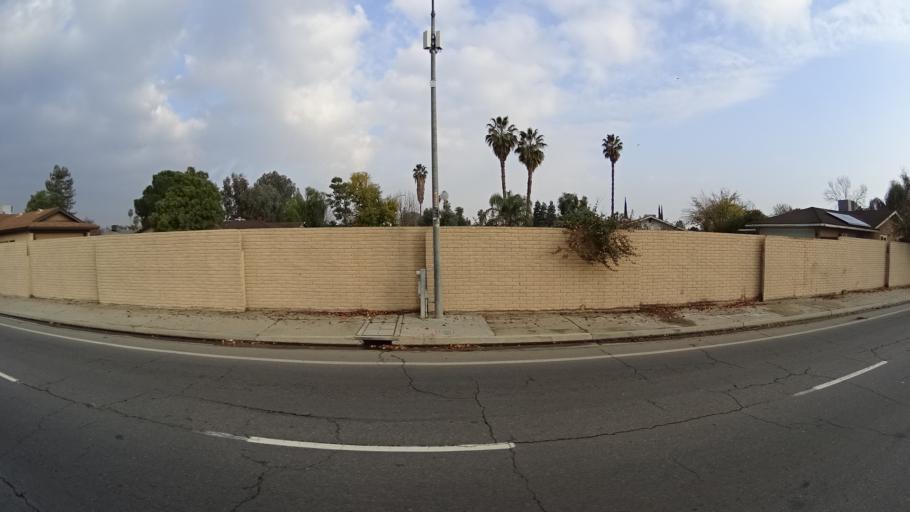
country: US
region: California
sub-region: Kern County
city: Bakersfield
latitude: 35.3182
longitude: -119.0668
